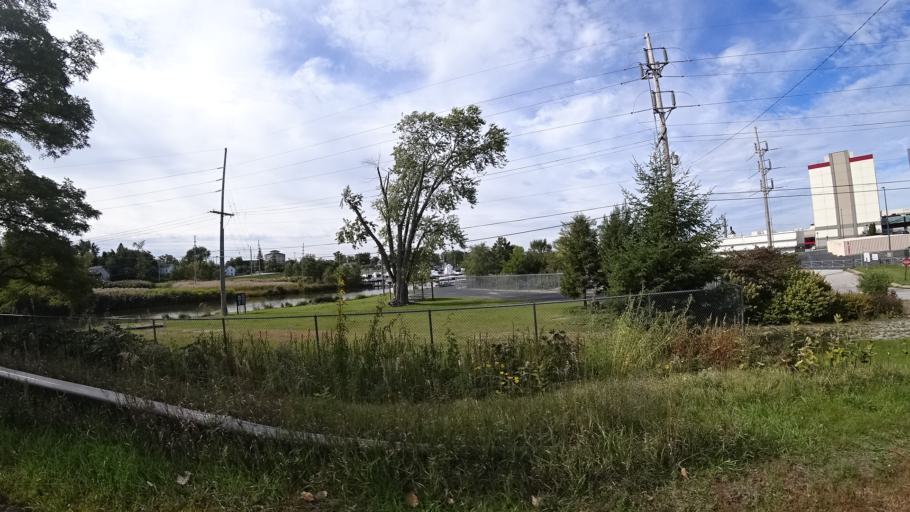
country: US
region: Indiana
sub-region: LaPorte County
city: Michigan City
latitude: 41.7175
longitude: -86.8895
